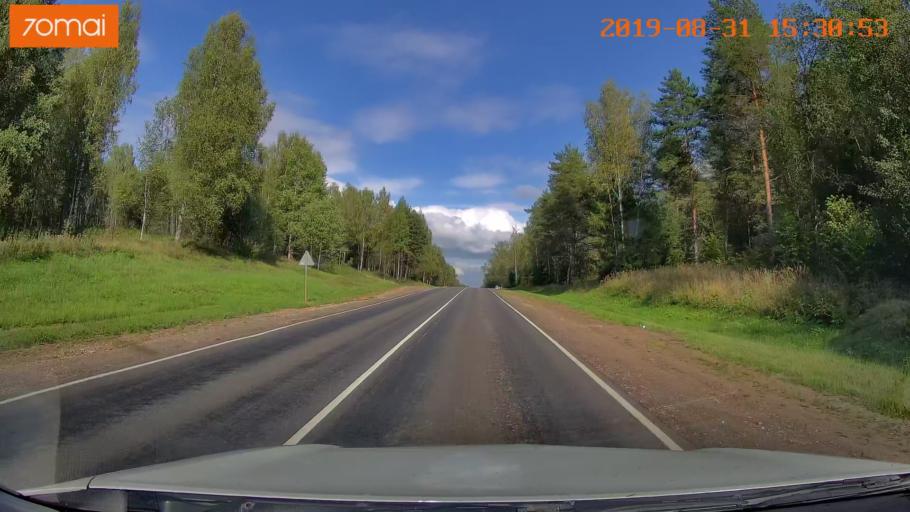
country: RU
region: Kaluga
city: Baryatino
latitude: 54.5786
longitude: 34.6409
